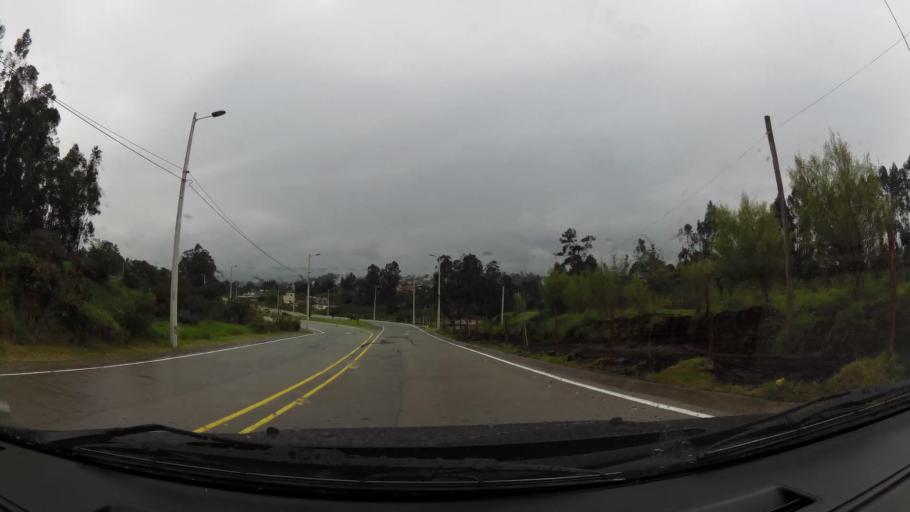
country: EC
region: Pichincha
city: Sangolqui
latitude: -0.2862
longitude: -78.4591
